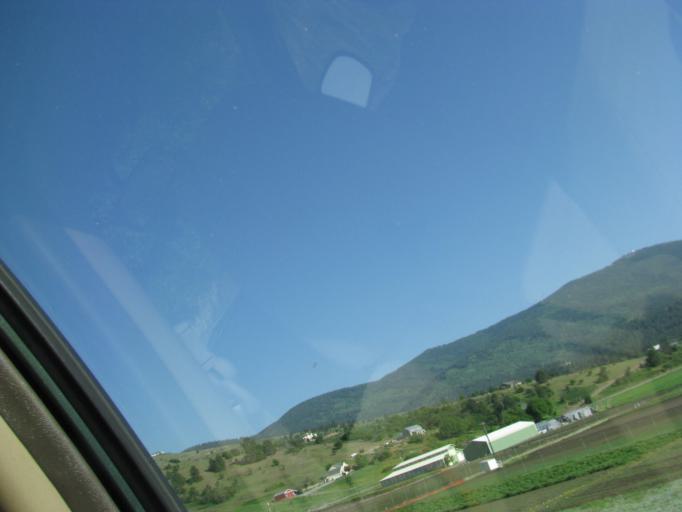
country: US
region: Washington
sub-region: Spokane County
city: Liberty Lake
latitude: 47.6288
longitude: -117.1174
